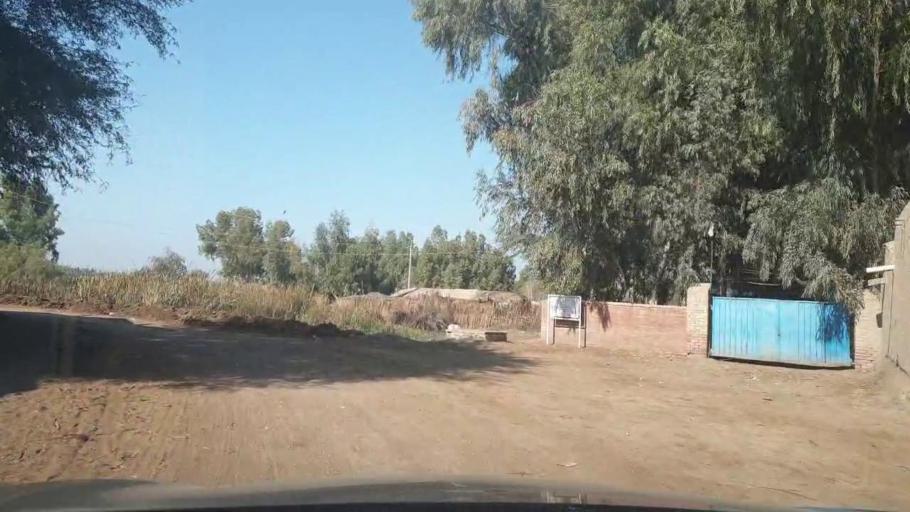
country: PK
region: Sindh
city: Khairpur
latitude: 28.1436
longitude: 69.6062
